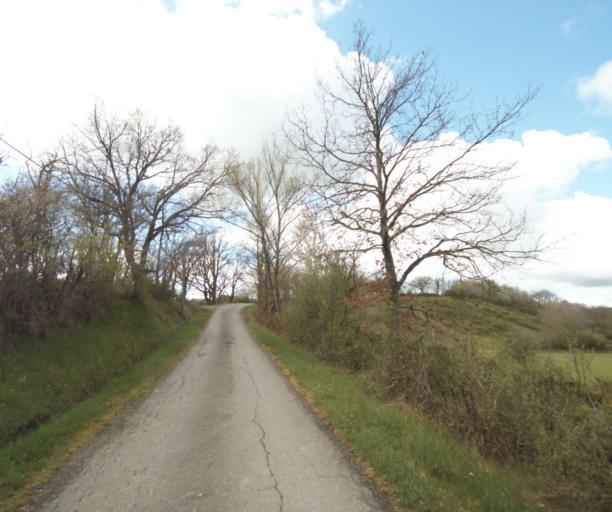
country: FR
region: Midi-Pyrenees
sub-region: Departement de l'Ariege
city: Saverdun
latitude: 43.2018
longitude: 1.5813
